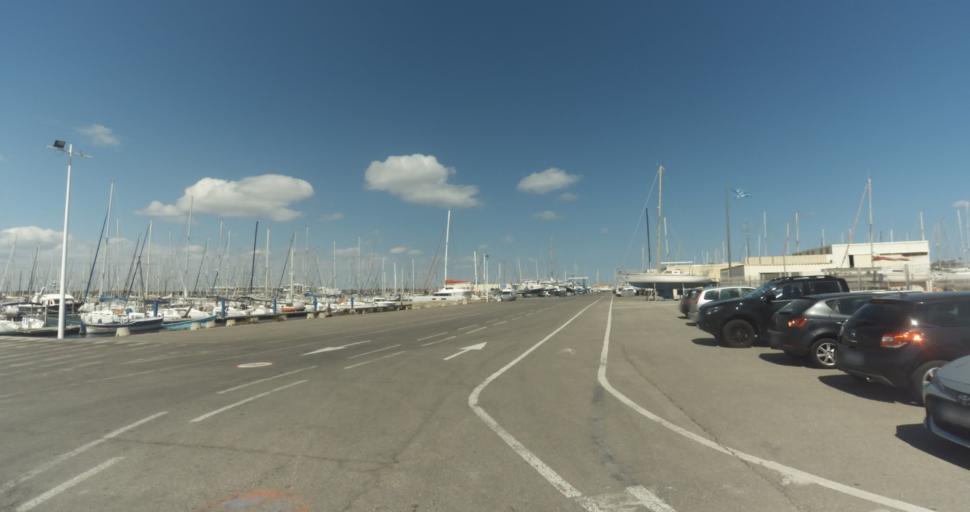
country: FR
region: Languedoc-Roussillon
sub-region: Departement de l'Aude
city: Leucate
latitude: 42.8638
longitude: 3.0412
